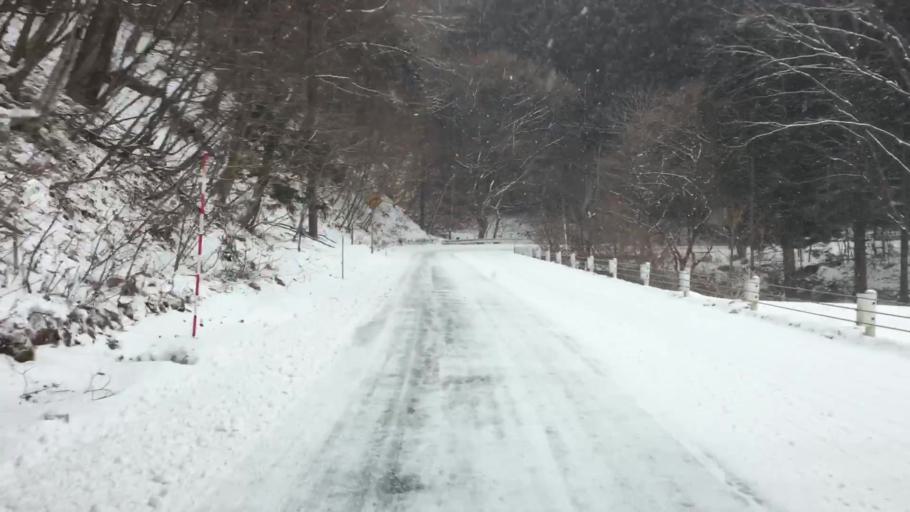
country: JP
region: Tochigi
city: Nikko
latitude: 36.8784
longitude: 139.7204
